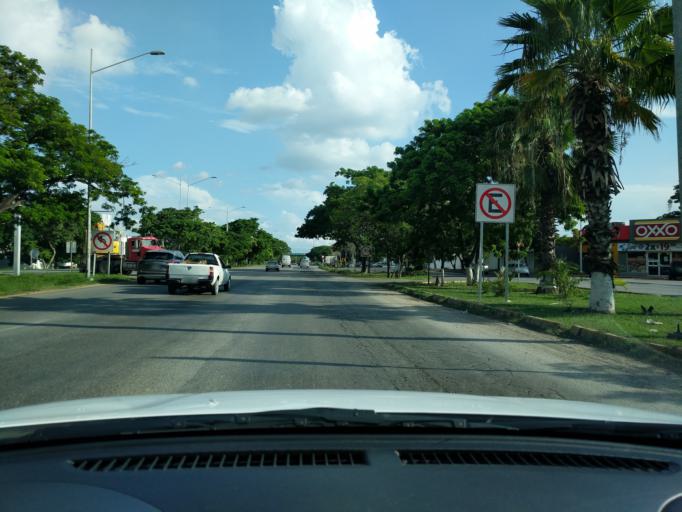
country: MX
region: Yucatan
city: Itzincab Palomeque
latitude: 20.9276
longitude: -89.6901
